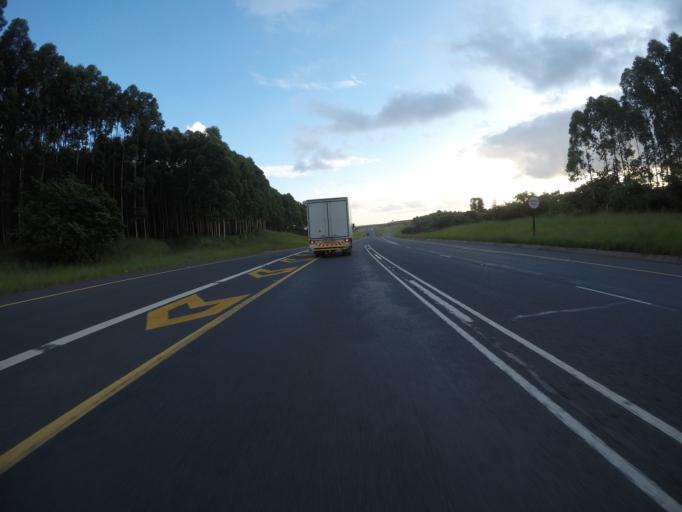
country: ZA
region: KwaZulu-Natal
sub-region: uThungulu District Municipality
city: KwaMbonambi
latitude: -28.5937
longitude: 32.0996
